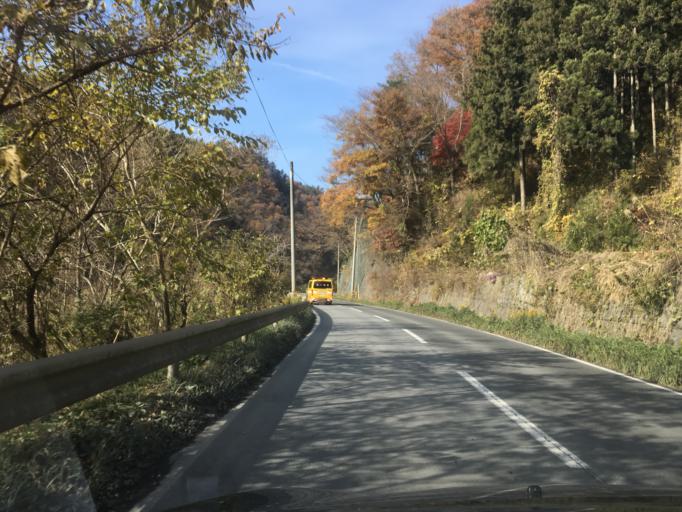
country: JP
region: Iwate
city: Ichinoseki
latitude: 38.9313
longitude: 141.2236
